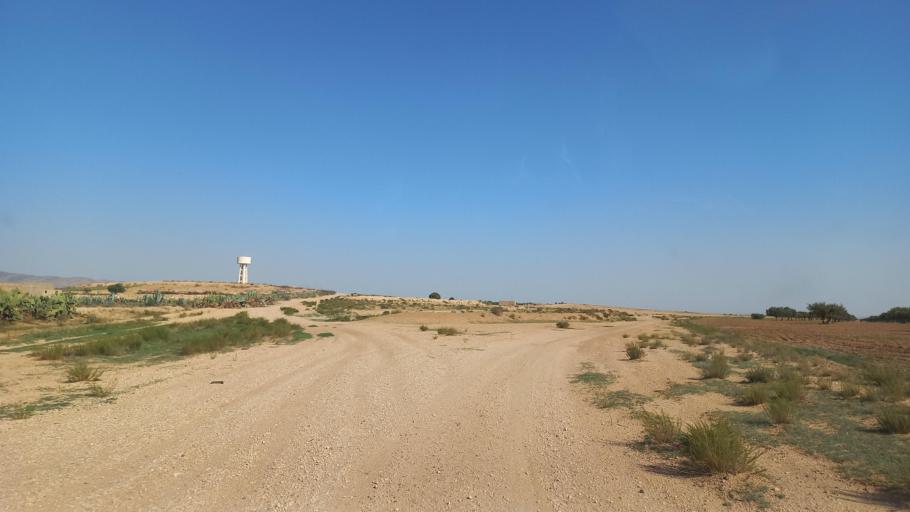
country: TN
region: Al Qasrayn
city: Kasserine
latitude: 35.3135
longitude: 9.0157
